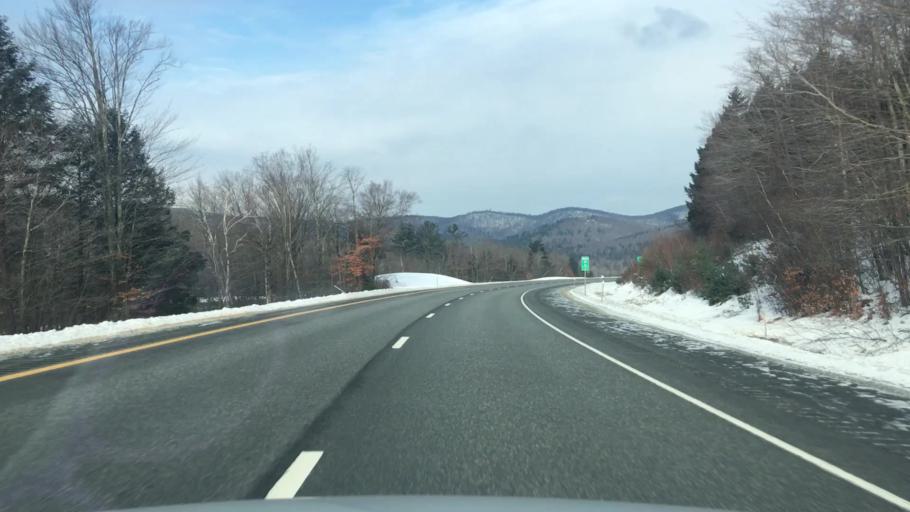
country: US
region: New Hampshire
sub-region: Sullivan County
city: Grantham
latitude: 43.4927
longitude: -72.1297
